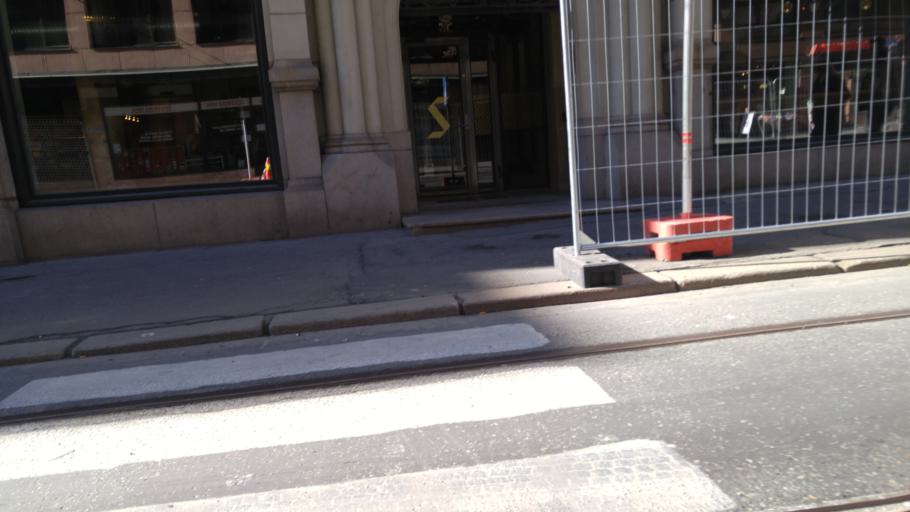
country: NO
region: Oslo
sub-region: Oslo
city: Oslo
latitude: 59.9114
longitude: 10.7402
